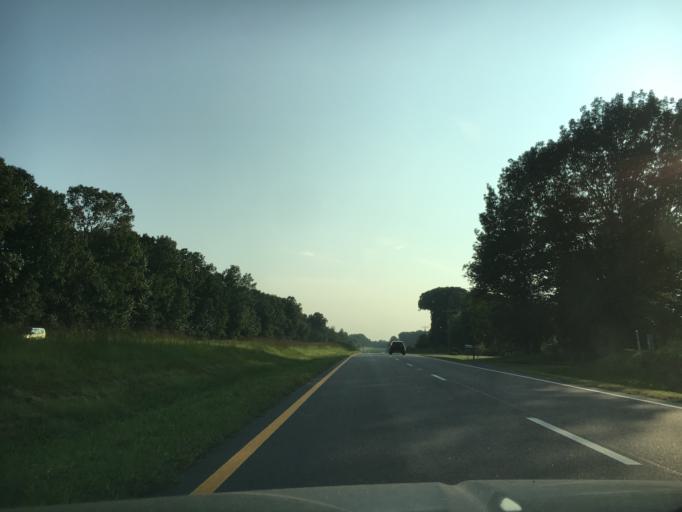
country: US
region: Virginia
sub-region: Prince Edward County
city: Hampden Sydney
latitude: 37.2727
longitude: -78.6388
